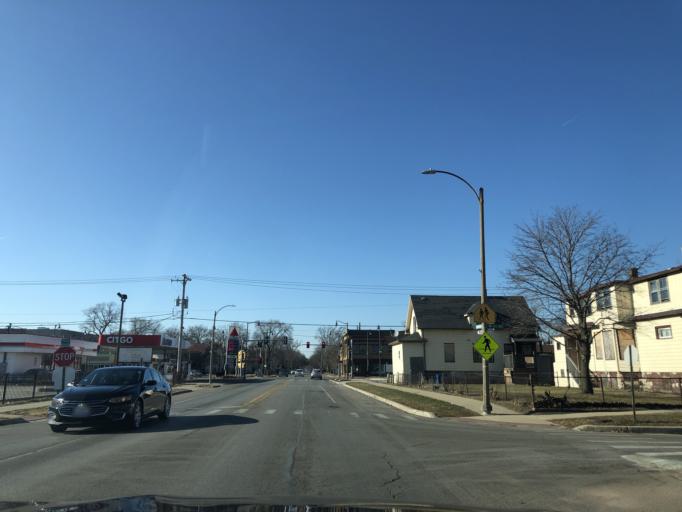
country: US
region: Illinois
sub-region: Cook County
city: Maywood
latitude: 41.8826
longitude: -87.8376
